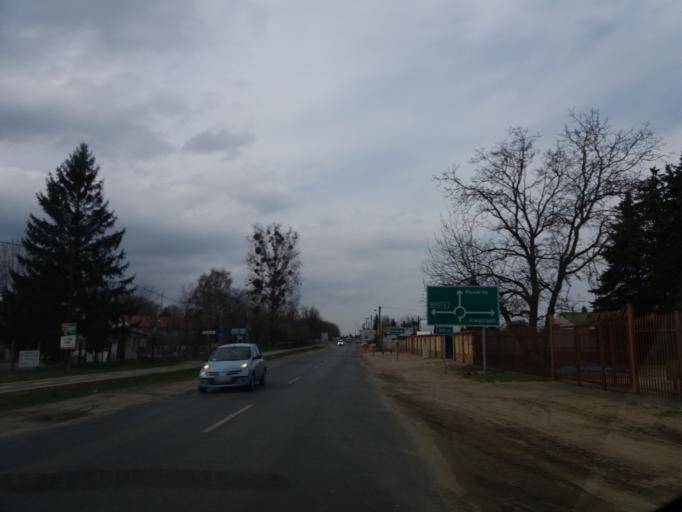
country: HU
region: Szabolcs-Szatmar-Bereg
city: Kisvarda
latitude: 48.1987
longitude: 22.0947
